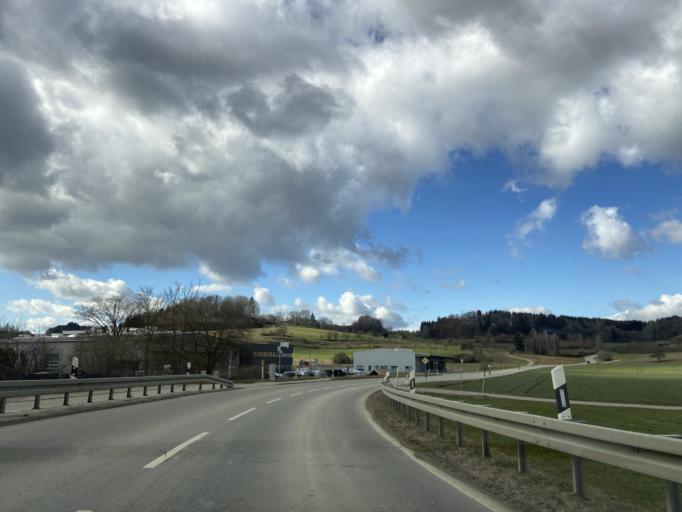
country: DE
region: Baden-Wuerttemberg
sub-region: Tuebingen Region
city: Krauchenwies
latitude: 48.0090
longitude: 9.1998
